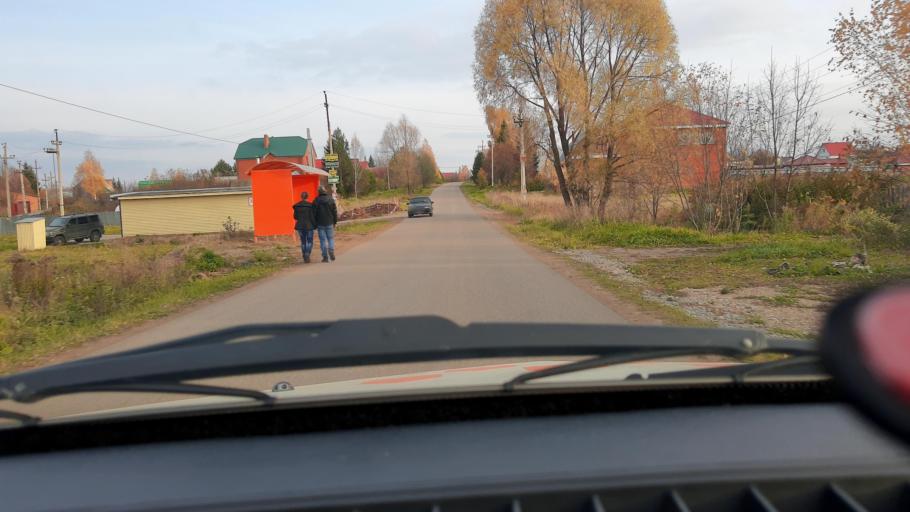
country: RU
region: Bashkortostan
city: Iglino
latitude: 54.7952
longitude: 56.3161
